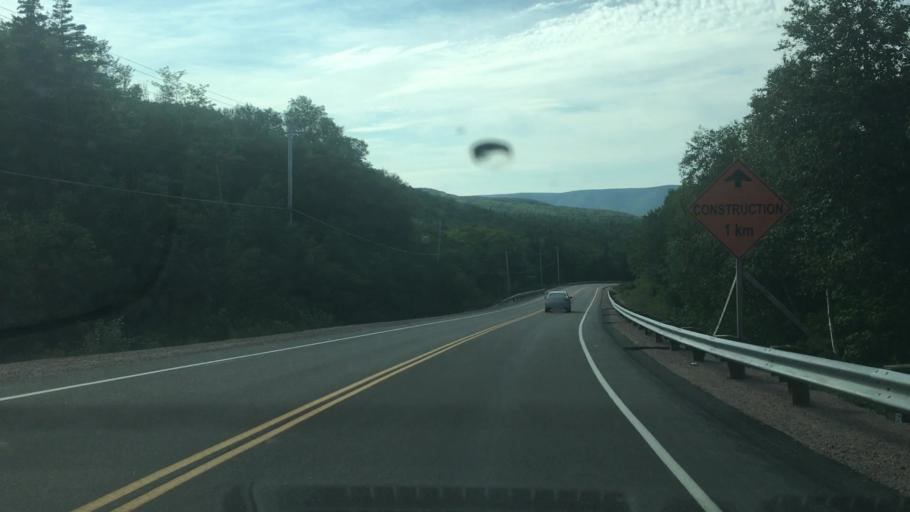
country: CA
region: Nova Scotia
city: Sydney Mines
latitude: 46.8551
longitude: -60.4541
